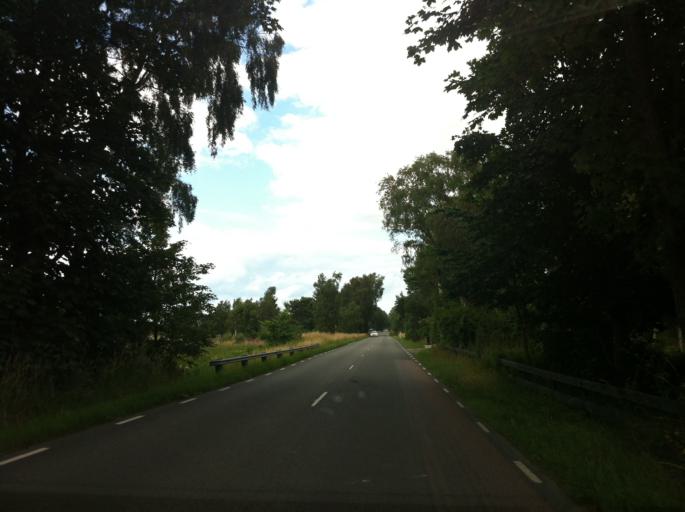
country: SE
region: Skane
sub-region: Simrishamns Kommun
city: Simrishamn
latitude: 55.4083
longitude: 14.1904
